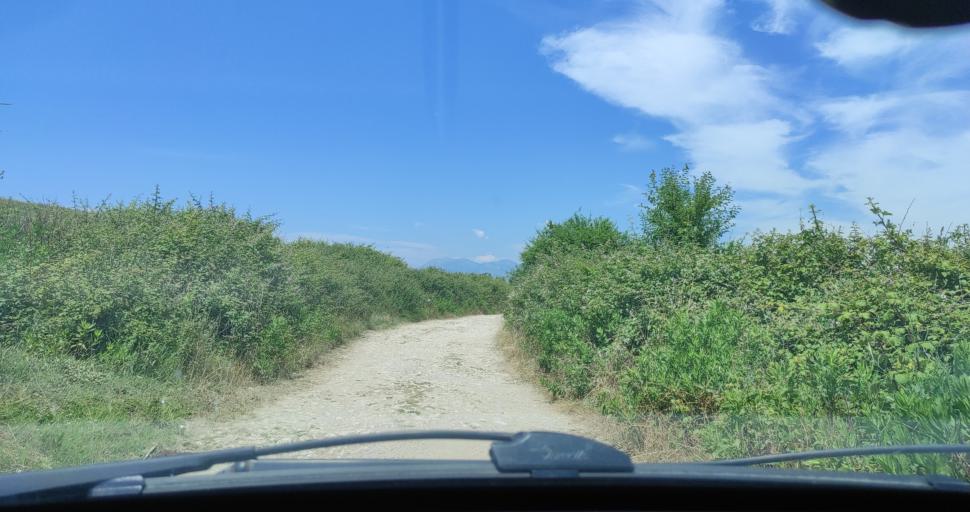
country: AL
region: Shkoder
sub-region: Rrethi i Shkodres
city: Velipoje
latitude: 41.8816
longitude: 19.3931
